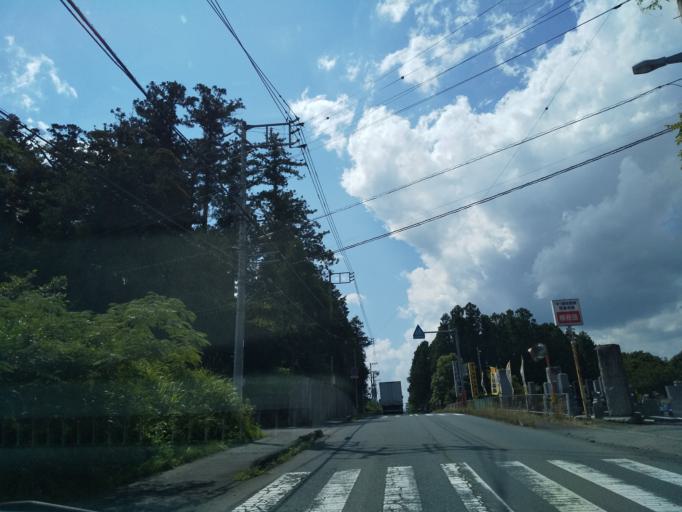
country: JP
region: Ibaraki
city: Ishioka
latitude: 36.1654
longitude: 140.3655
